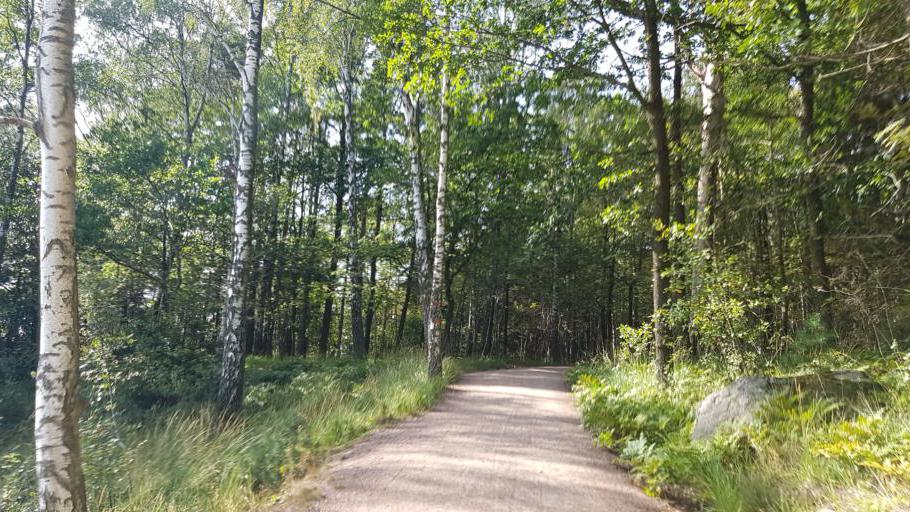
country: SE
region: Vaestra Goetaland
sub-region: Molndal
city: Moelndal
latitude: 57.6896
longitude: 12.0451
